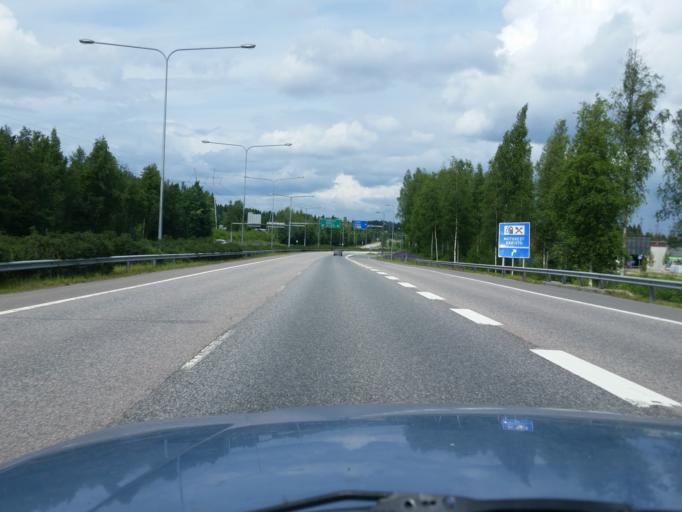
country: FI
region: Paijanne Tavastia
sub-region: Lahti
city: Lahti
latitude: 60.9797
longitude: 25.7315
